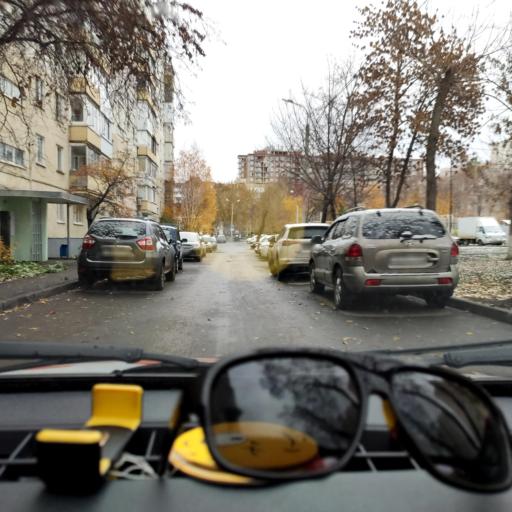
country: RU
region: Bashkortostan
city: Ufa
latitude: 54.7118
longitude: 55.9719
